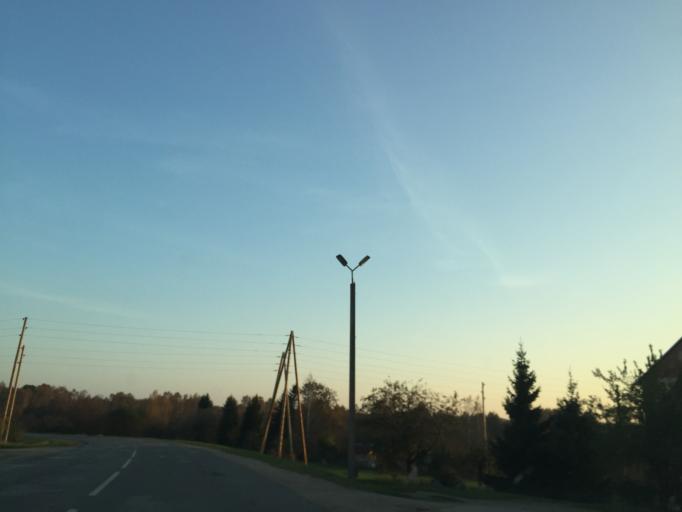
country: LV
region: Priekule
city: Priekule
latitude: 56.4376
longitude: 21.5835
